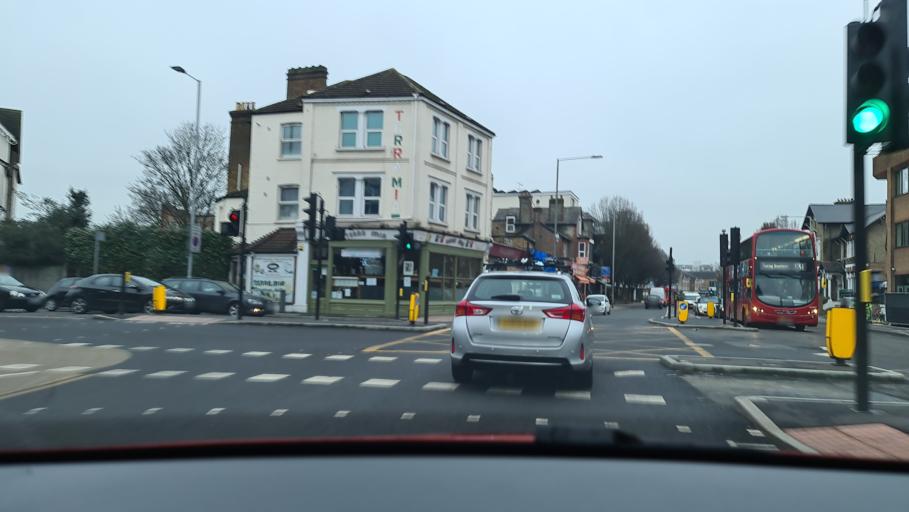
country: GB
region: England
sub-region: Greater London
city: Kingston upon Thames
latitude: 51.4109
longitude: -0.2916
